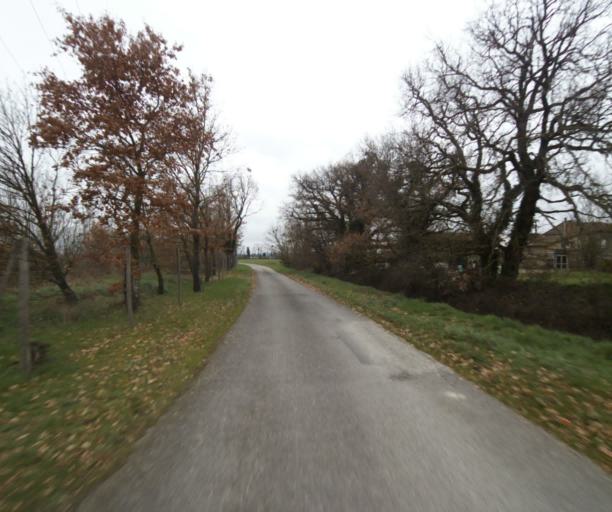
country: FR
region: Midi-Pyrenees
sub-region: Departement de l'Ariege
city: Saverdun
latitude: 43.2252
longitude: 1.6171
